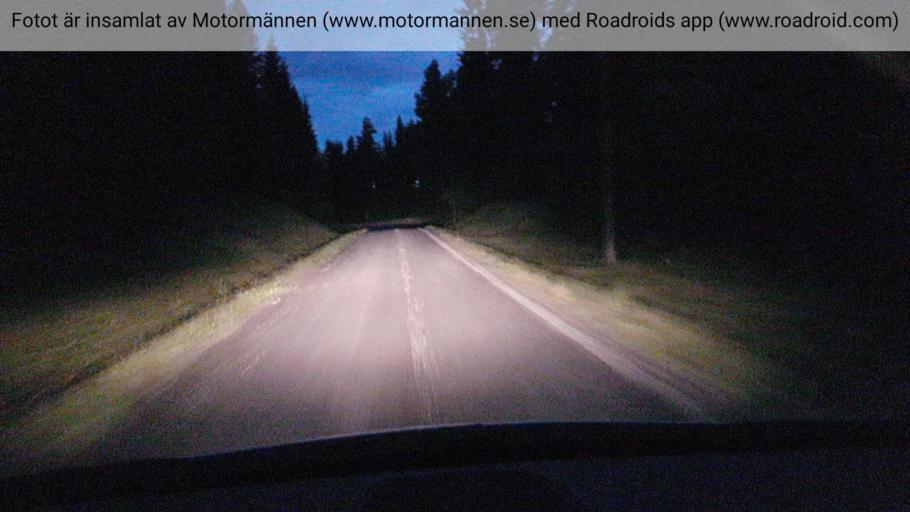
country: SE
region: Jaemtland
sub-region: OEstersunds Kommun
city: Lit
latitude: 63.3040
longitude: 15.2920
